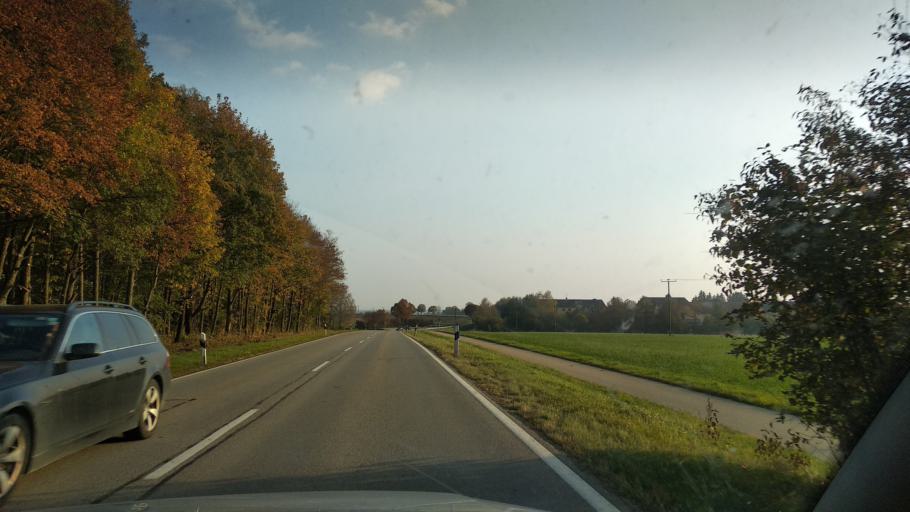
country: DE
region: Bavaria
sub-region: Upper Bavaria
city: Pastetten
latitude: 48.2239
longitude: 11.9450
